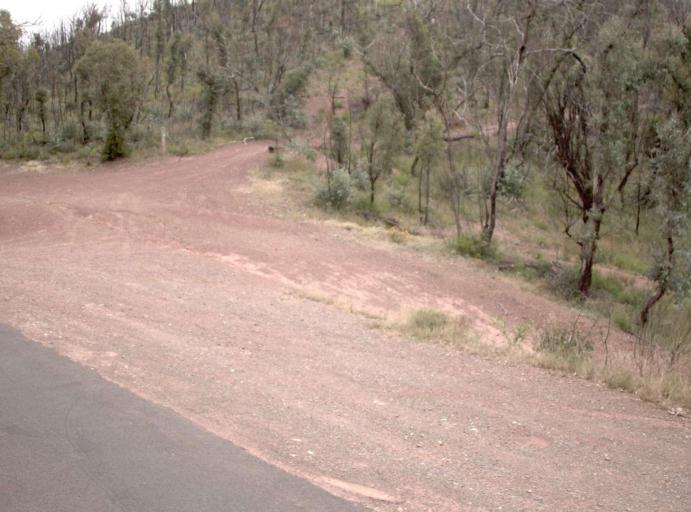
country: AU
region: Victoria
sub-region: Wellington
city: Heyfield
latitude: -37.7142
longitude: 146.6688
